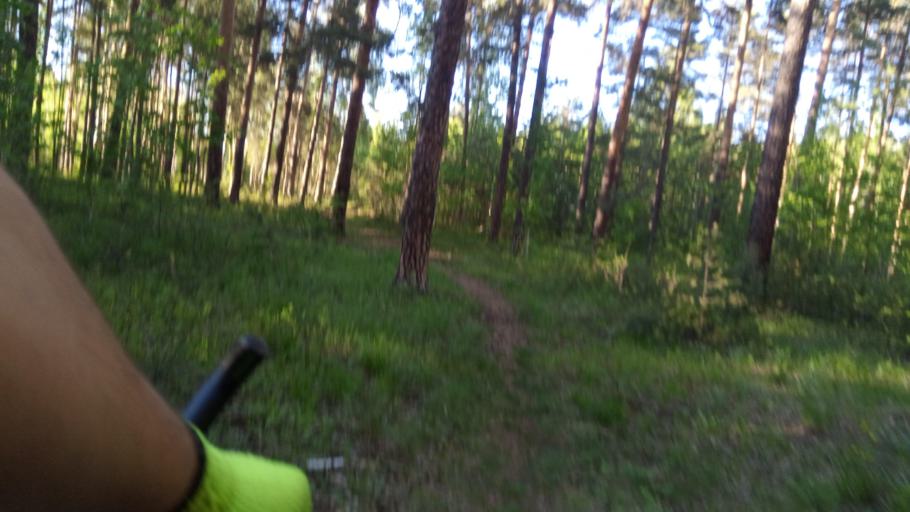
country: RU
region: Chelyabinsk
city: Novosineglazovskiy
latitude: 55.1236
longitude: 61.3432
